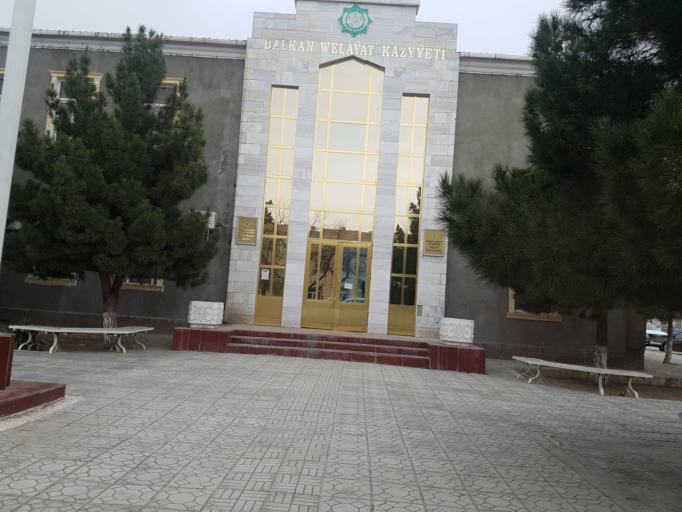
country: TM
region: Balkan
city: Balkanabat
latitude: 39.5064
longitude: 54.3584
